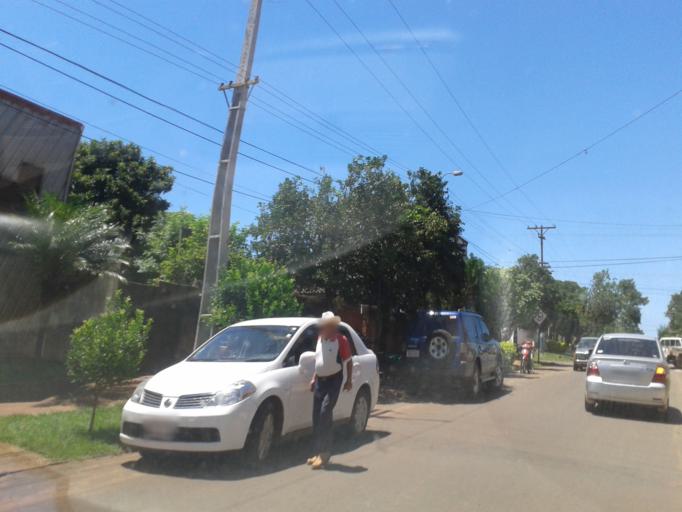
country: PY
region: Misiones
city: Santa Maria
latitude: -26.8878
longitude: -57.0259
